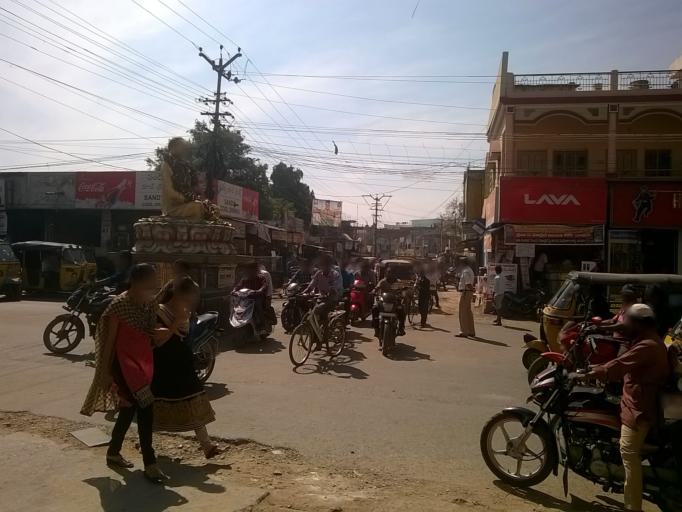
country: IN
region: Andhra Pradesh
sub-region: Kurnool
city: Nandyal
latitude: 15.4853
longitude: 78.4864
